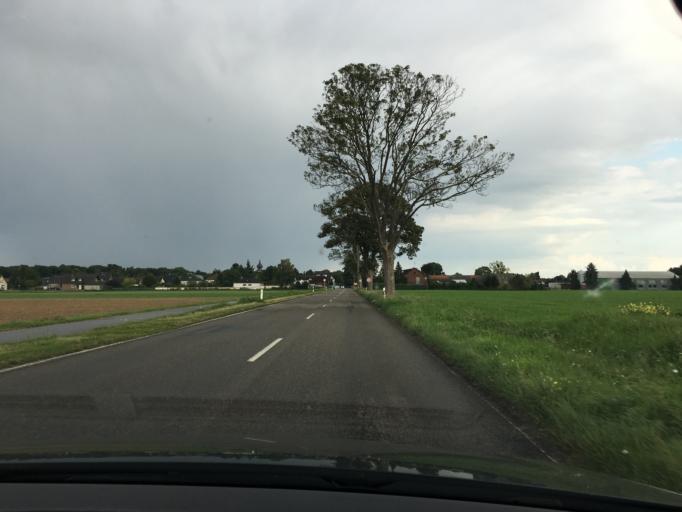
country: DE
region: North Rhine-Westphalia
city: Tuernich
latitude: 50.8436
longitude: 6.7299
